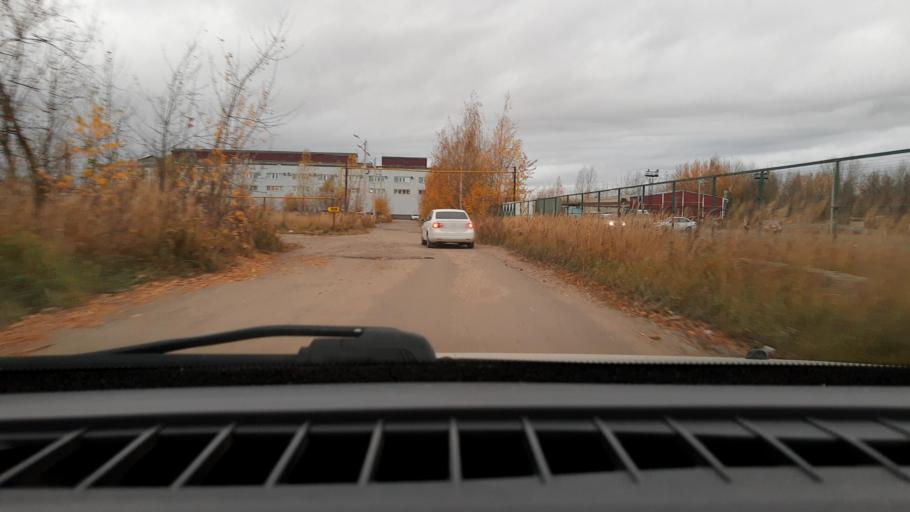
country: RU
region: Nizjnij Novgorod
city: Nizhniy Novgorod
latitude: 56.3338
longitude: 43.8997
